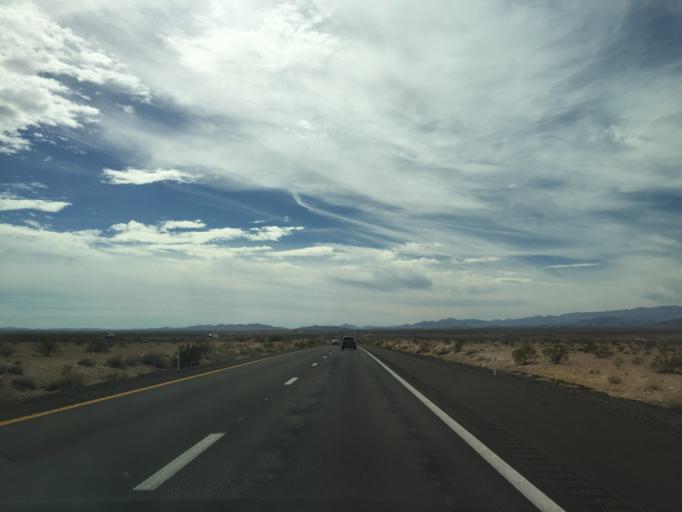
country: US
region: Nevada
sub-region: Clark County
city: Moapa Town
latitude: 36.5722
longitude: -114.6687
